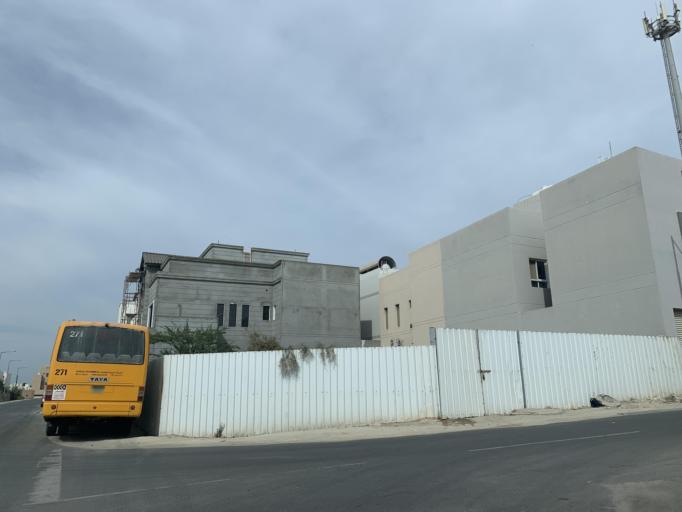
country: BH
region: Central Governorate
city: Madinat Hamad
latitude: 26.1179
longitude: 50.4782
